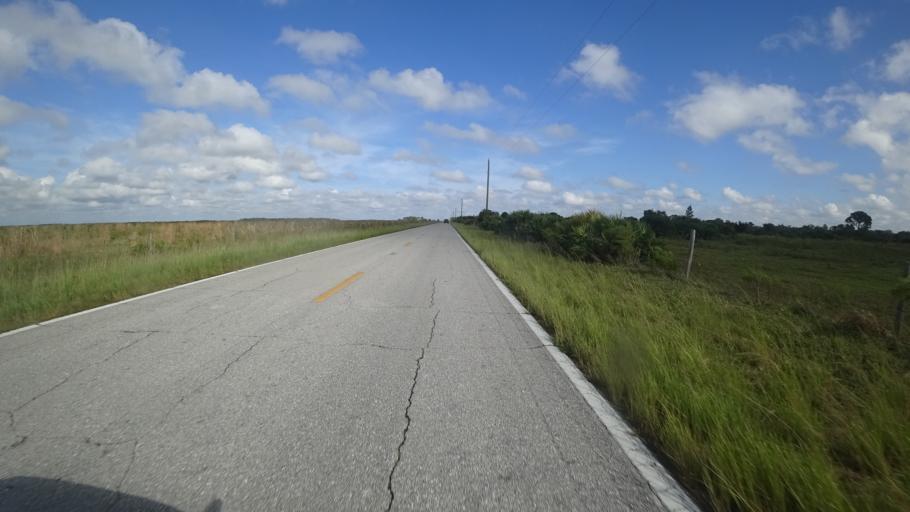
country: US
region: Florida
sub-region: Hardee County
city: Wauchula
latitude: 27.5037
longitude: -82.0715
